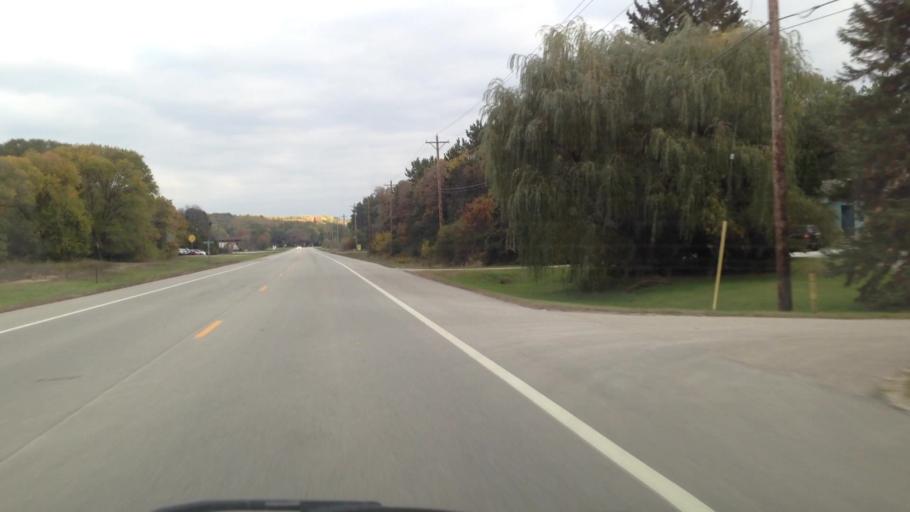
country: US
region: Minnesota
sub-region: Olmsted County
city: Rochester
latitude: 43.9883
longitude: -92.4123
